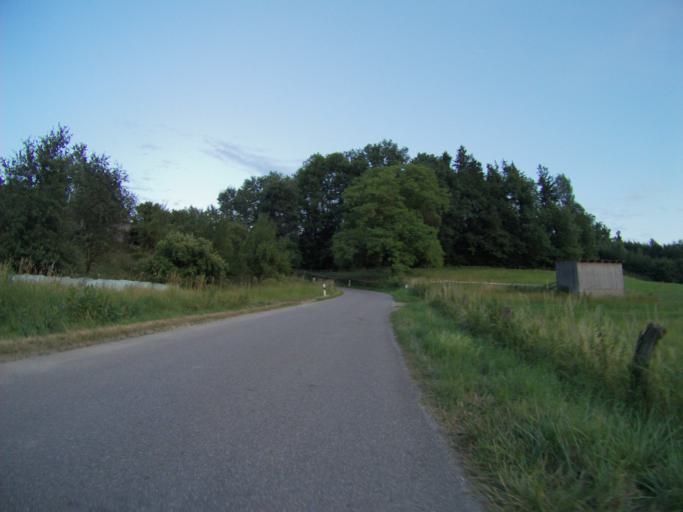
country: DE
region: Bavaria
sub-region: Upper Bavaria
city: Marzling
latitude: 48.4373
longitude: 11.7971
